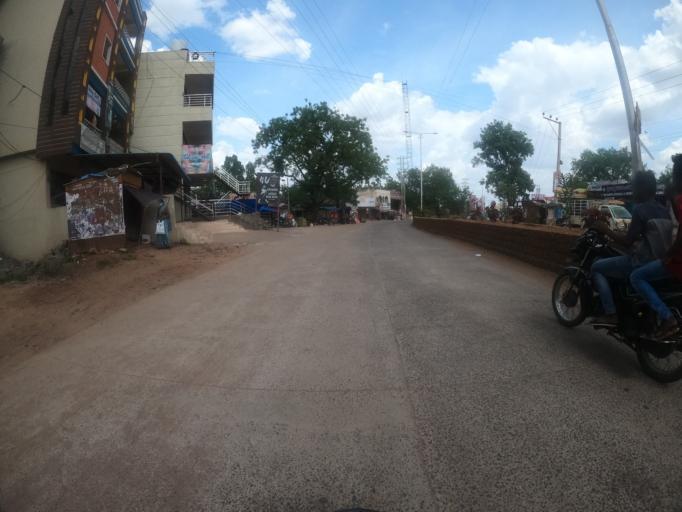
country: IN
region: Telangana
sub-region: Rangareddi
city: Sriramnagar
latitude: 17.3146
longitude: 78.1388
